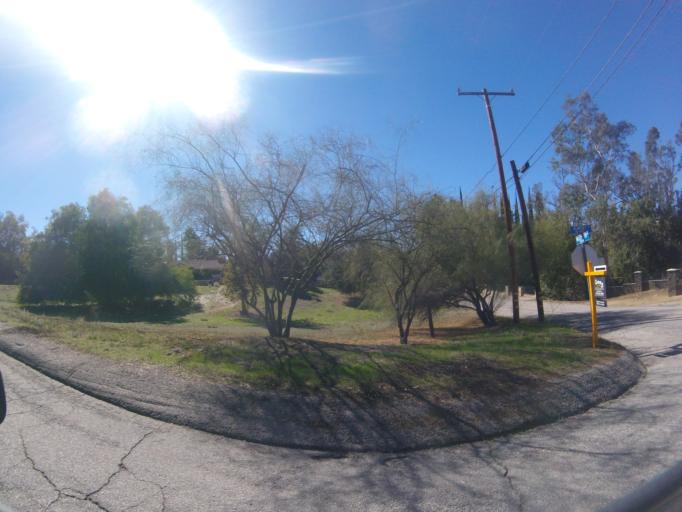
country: US
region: California
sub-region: San Bernardino County
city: Mentone
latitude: 34.0244
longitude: -117.1274
